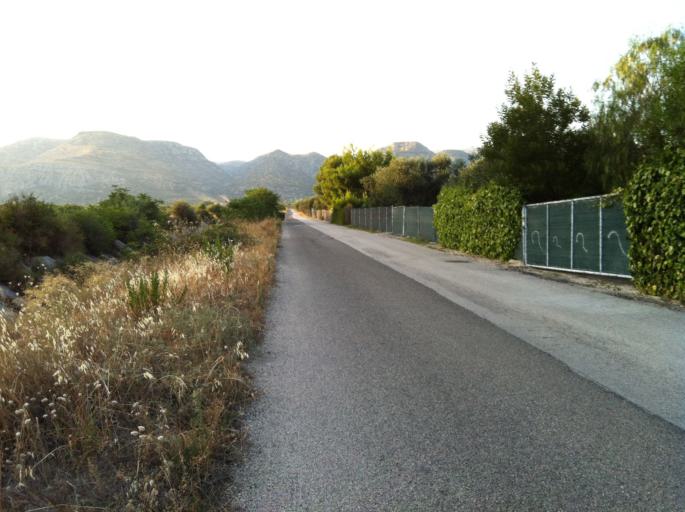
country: IT
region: Apulia
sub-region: Provincia di Foggia
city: Manfredonia
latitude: 41.6547
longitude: 15.9523
